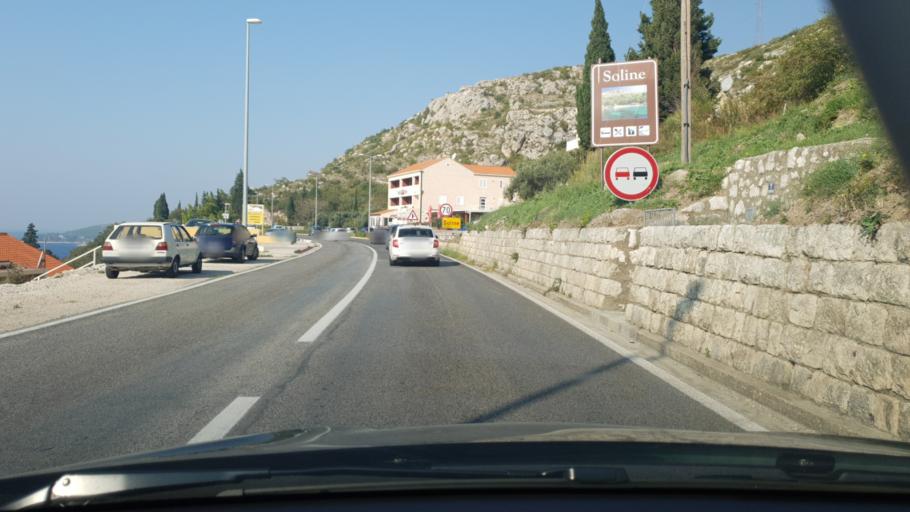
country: HR
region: Dubrovacko-Neretvanska
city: Cavtat
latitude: 42.6142
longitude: 18.2232
